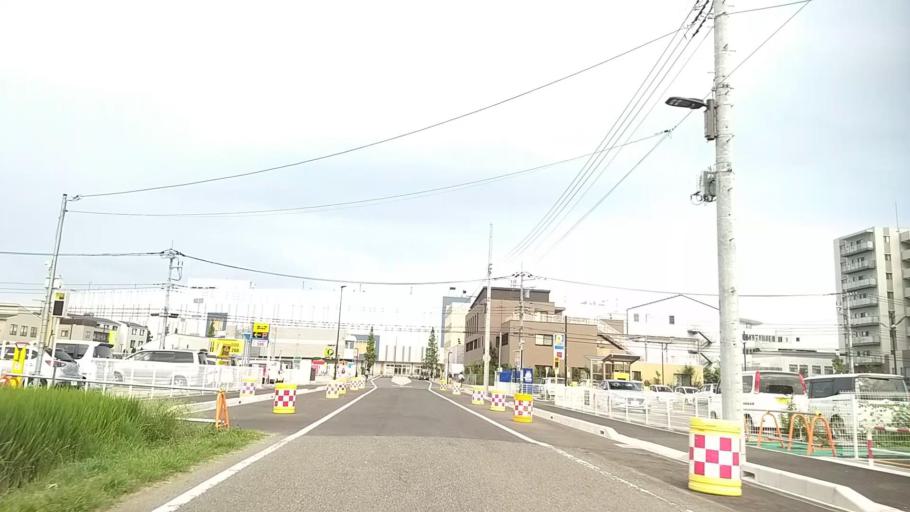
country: JP
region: Kanagawa
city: Atsugi
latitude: 35.4560
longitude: 139.3864
